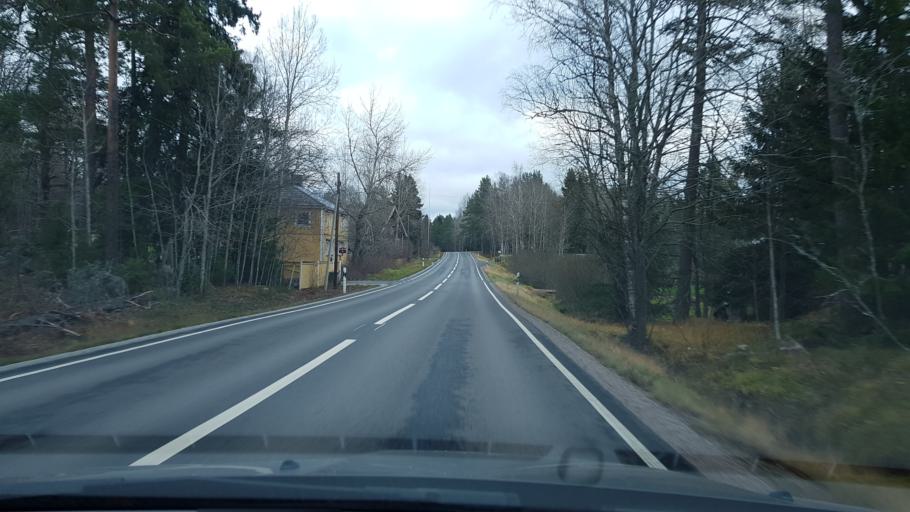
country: SE
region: Stockholm
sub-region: Norrtalje Kommun
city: Skanninge
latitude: 60.0207
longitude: 18.3997
